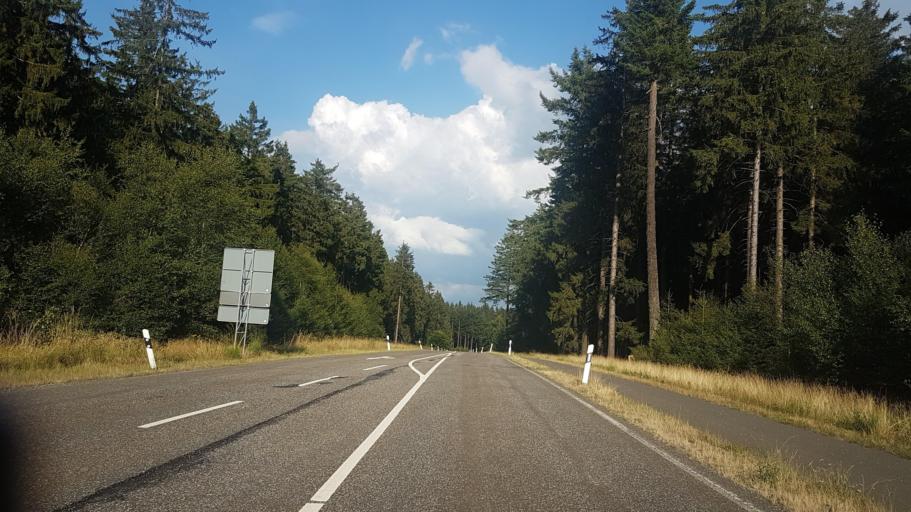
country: DE
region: Rheinland-Pfalz
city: Deuselbach
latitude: 49.7386
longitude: 7.1047
